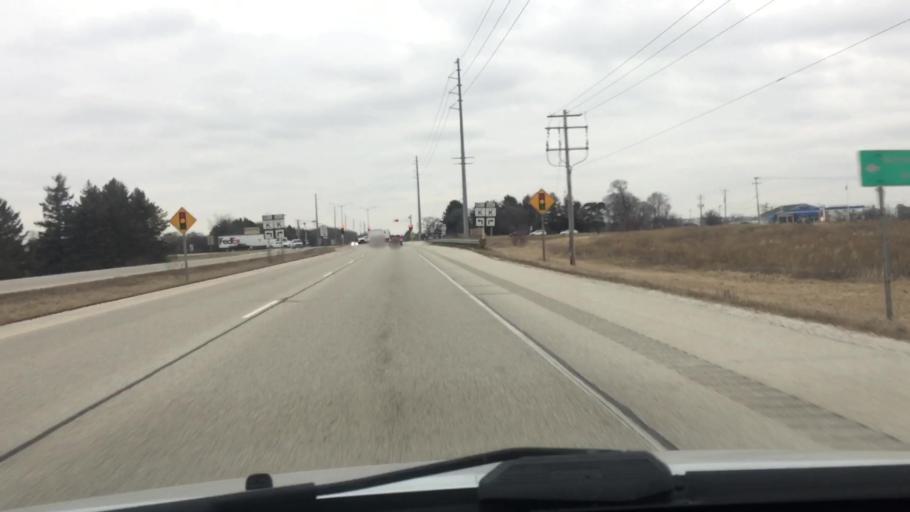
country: US
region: Wisconsin
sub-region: Waukesha County
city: Sussex
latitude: 43.1099
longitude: -88.2102
